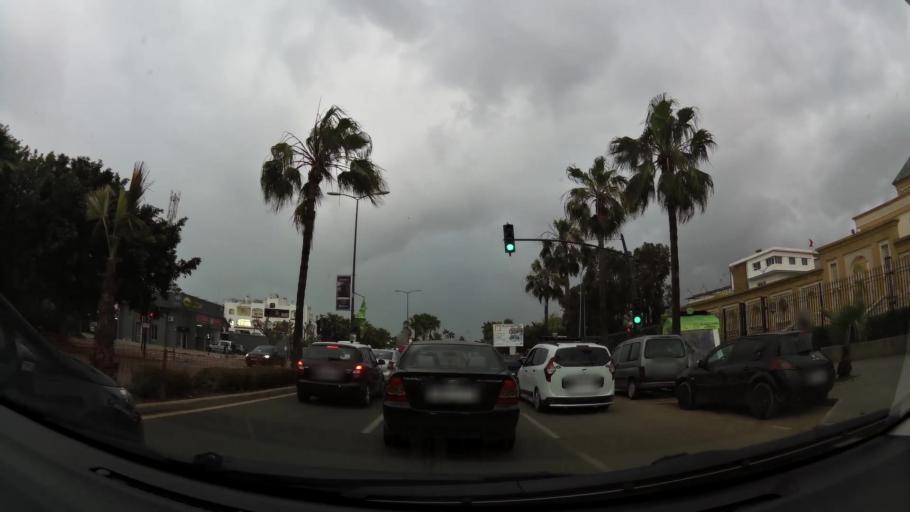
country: MA
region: Grand Casablanca
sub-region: Casablanca
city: Casablanca
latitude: 33.5744
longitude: -7.6820
